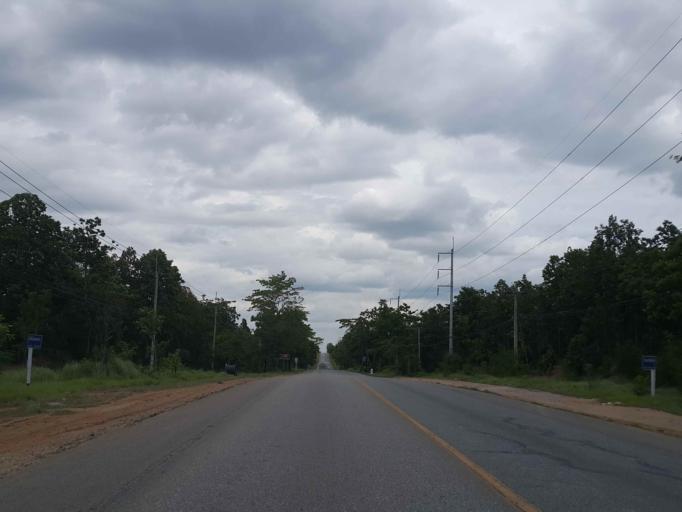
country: TH
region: Lamphun
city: Ban Hong
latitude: 18.4074
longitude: 98.8431
